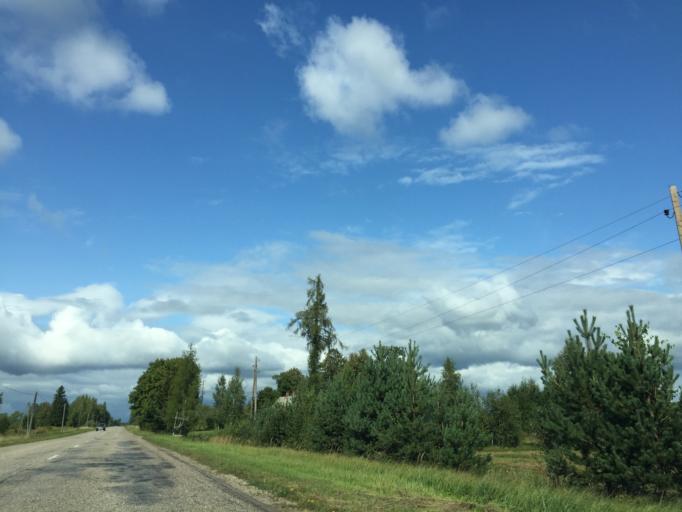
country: LV
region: Pargaujas
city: Stalbe
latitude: 57.4129
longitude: 24.9536
